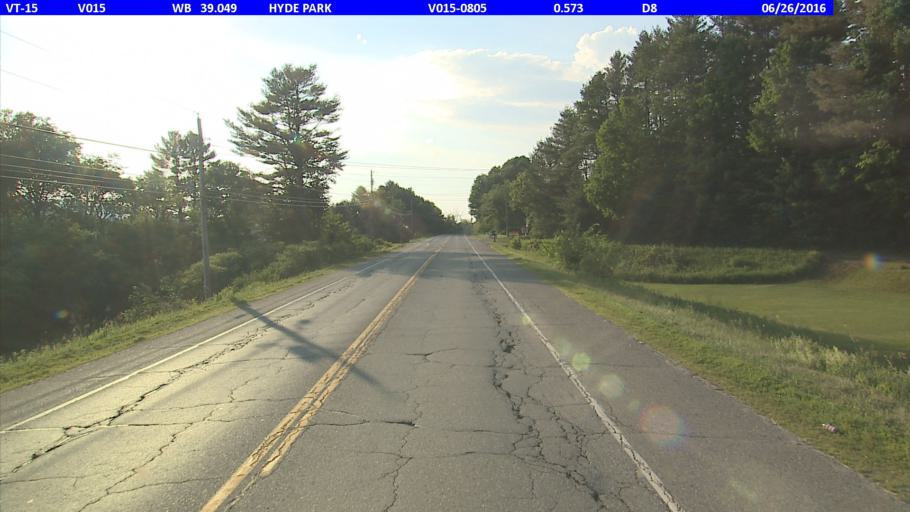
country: US
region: Vermont
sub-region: Lamoille County
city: Hyde Park
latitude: 44.6027
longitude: -72.6396
